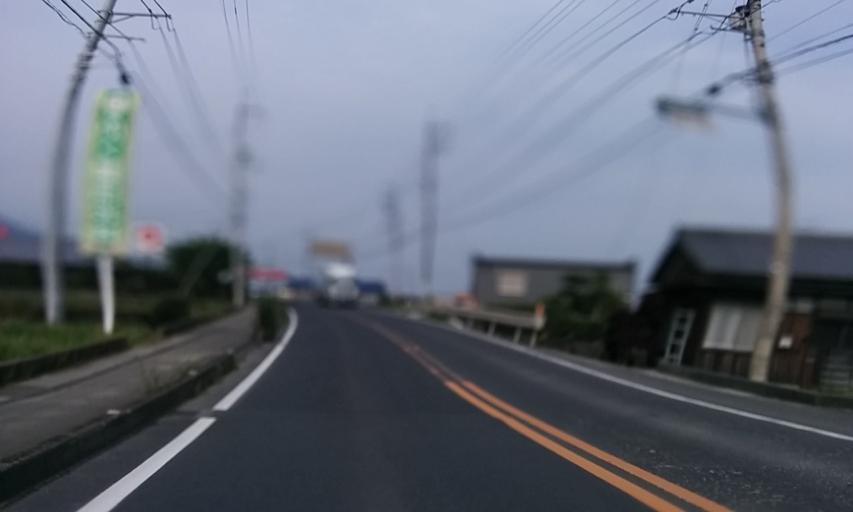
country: JP
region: Ehime
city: Kawanoecho
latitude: 33.9649
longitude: 133.4663
